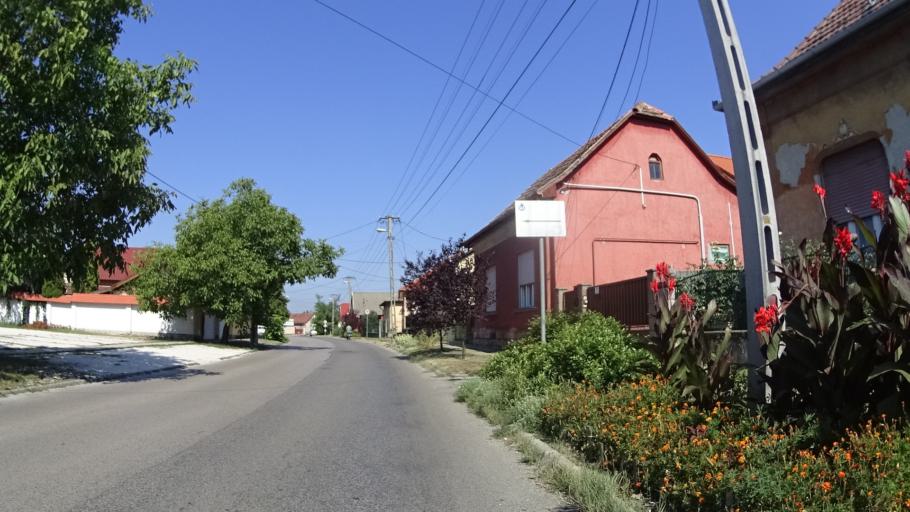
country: HU
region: Pest
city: Dunakeszi
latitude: 47.6331
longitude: 19.1323
